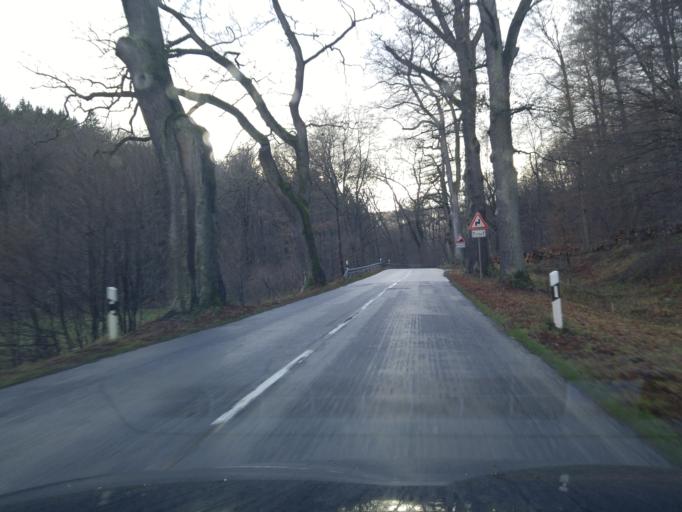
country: DE
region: Hesse
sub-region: Regierungsbezirk Kassel
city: Udenhausen
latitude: 51.4893
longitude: 9.5568
